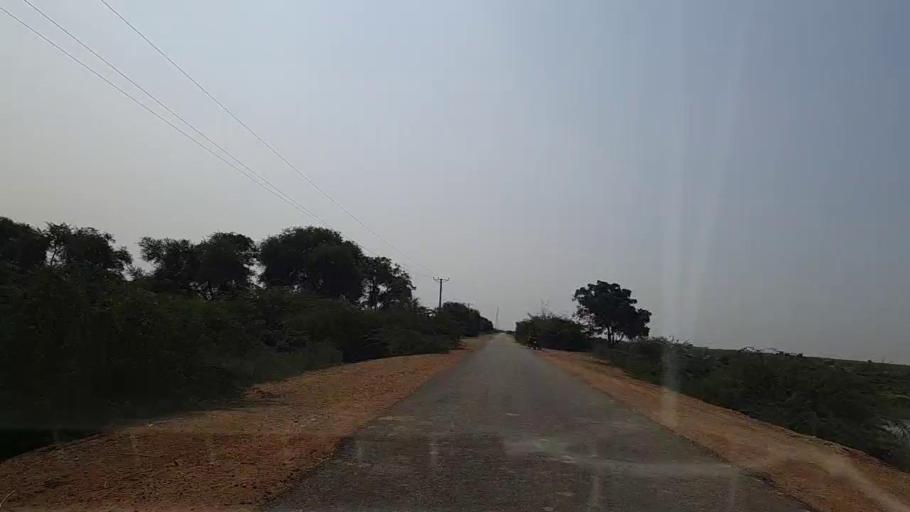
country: PK
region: Sindh
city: Chuhar Jamali
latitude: 24.2962
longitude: 67.9300
